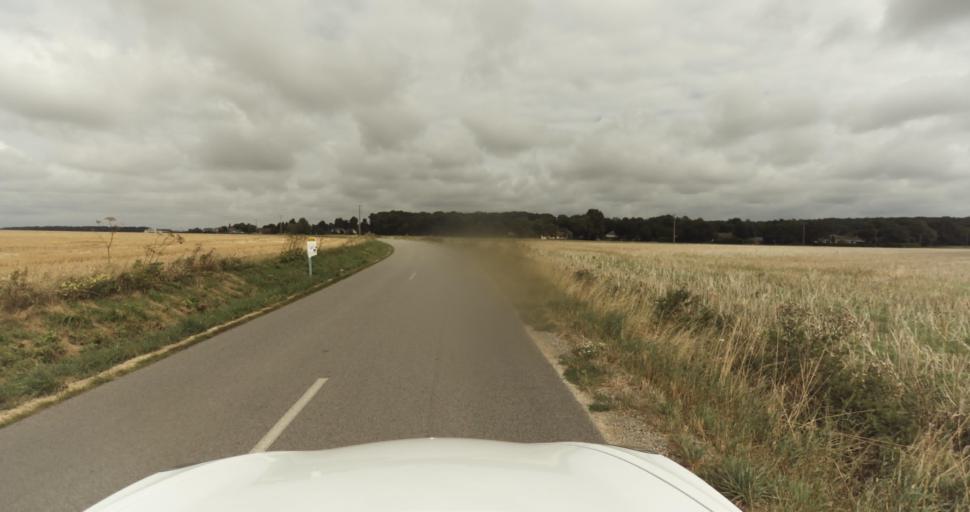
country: FR
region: Haute-Normandie
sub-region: Departement de l'Eure
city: Claville
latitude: 49.0166
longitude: 1.0345
